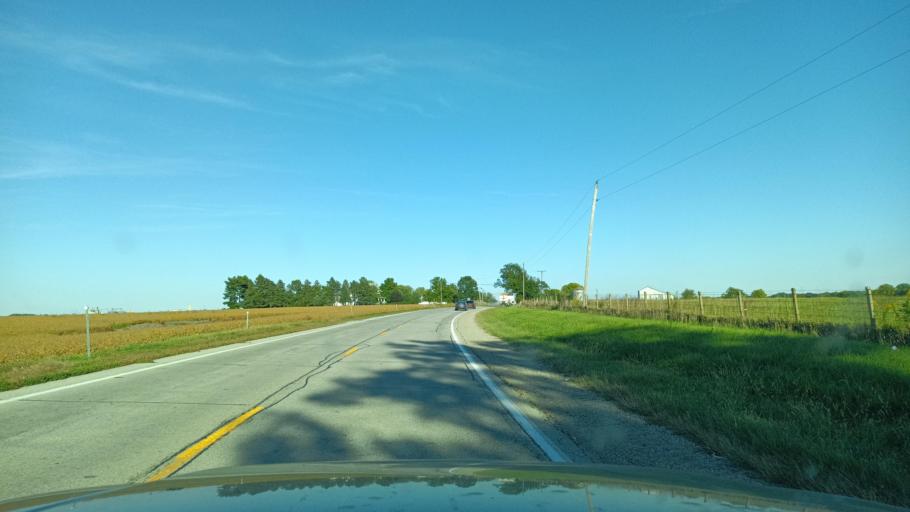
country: US
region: Illinois
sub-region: De Witt County
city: Farmer City
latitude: 40.2316
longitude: -88.6759
